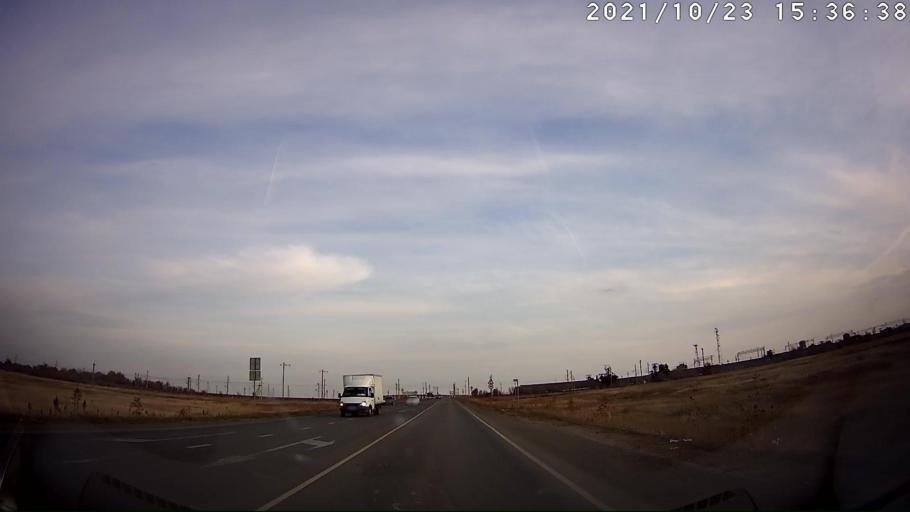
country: RU
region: Volgograd
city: Bereslavka
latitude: 48.1474
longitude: 44.1196
